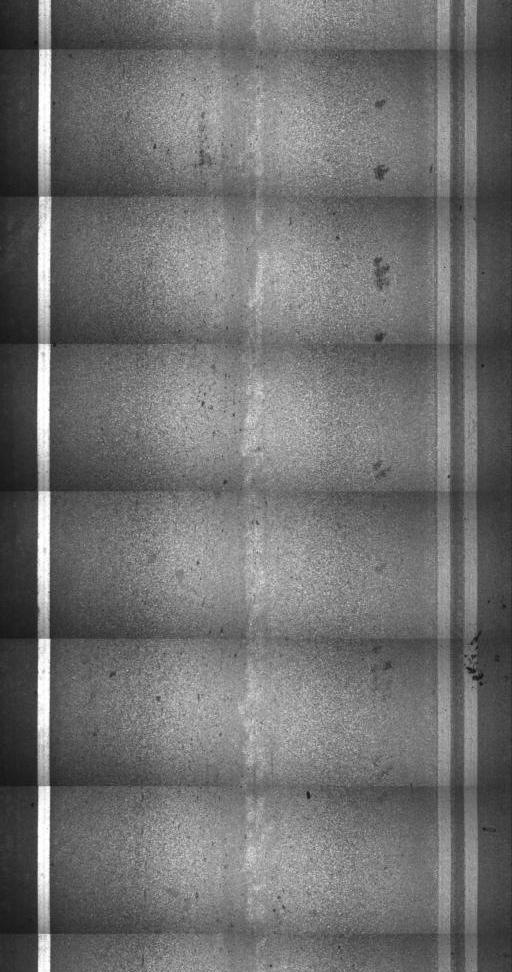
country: US
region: Vermont
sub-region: Franklin County
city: Swanton
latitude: 44.9433
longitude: -73.0100
